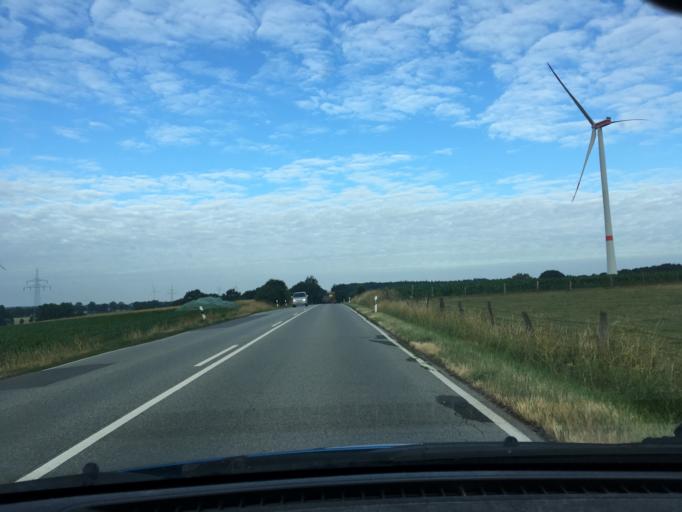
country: DE
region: Lower Saxony
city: Wulfsen
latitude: 53.3161
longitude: 10.1178
